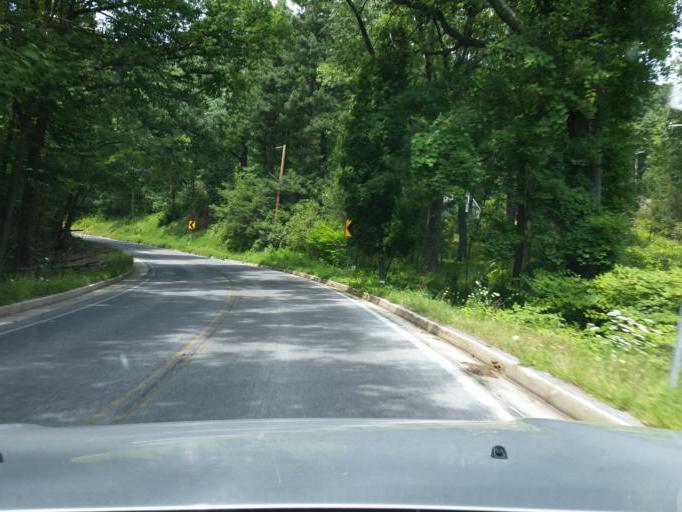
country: US
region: Pennsylvania
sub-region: Blair County
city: Altoona
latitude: 40.5554
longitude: -78.4433
